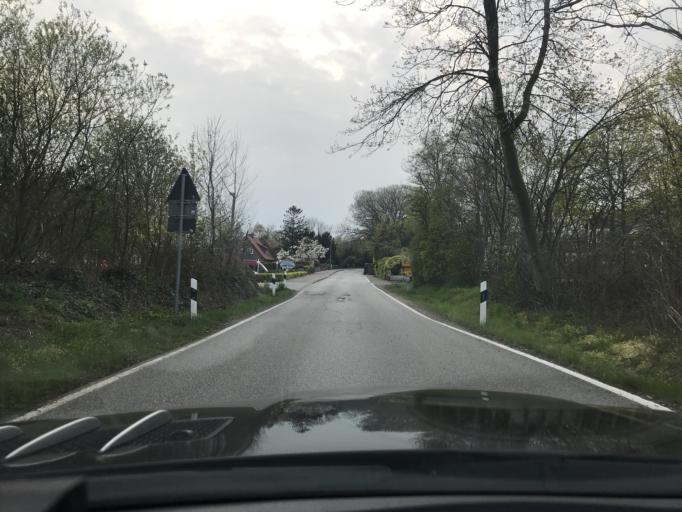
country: DE
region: Schleswig-Holstein
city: Burg auf Fehmarn
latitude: 54.4229
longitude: 11.2547
